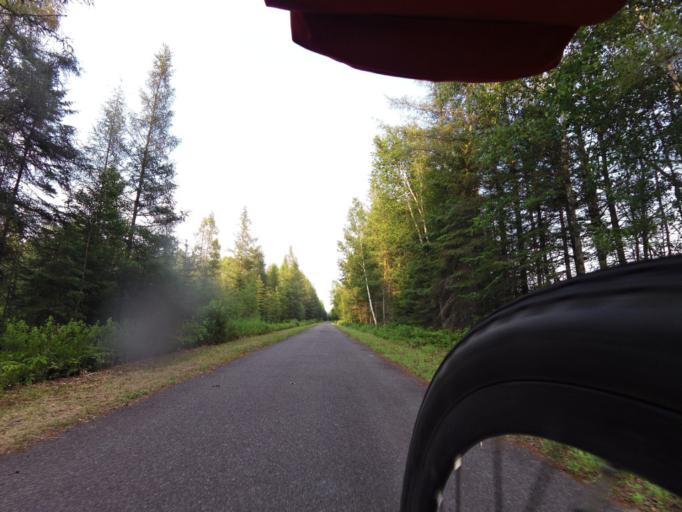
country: CA
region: Quebec
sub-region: Laurentides
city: Riviere-Rouge
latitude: 46.3939
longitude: -75.0238
